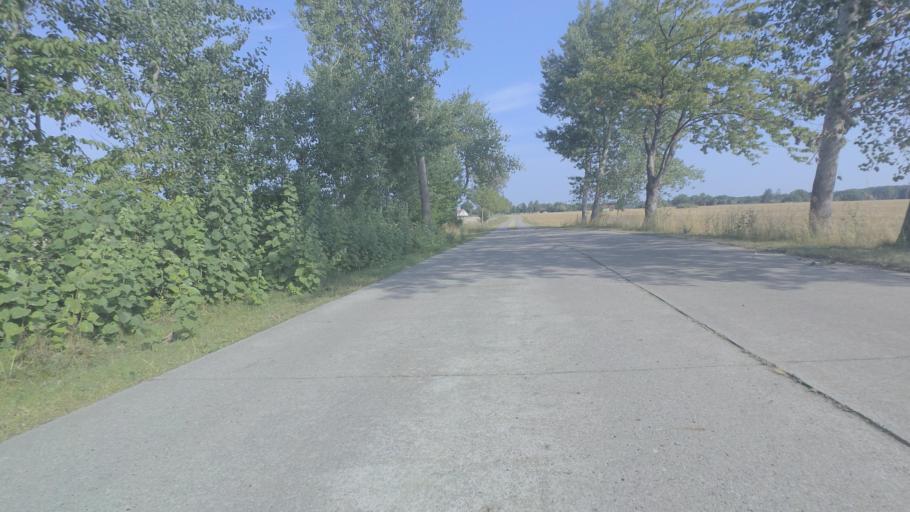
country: DE
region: Mecklenburg-Vorpommern
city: Wittenhagen
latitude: 54.1791
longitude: 13.0748
